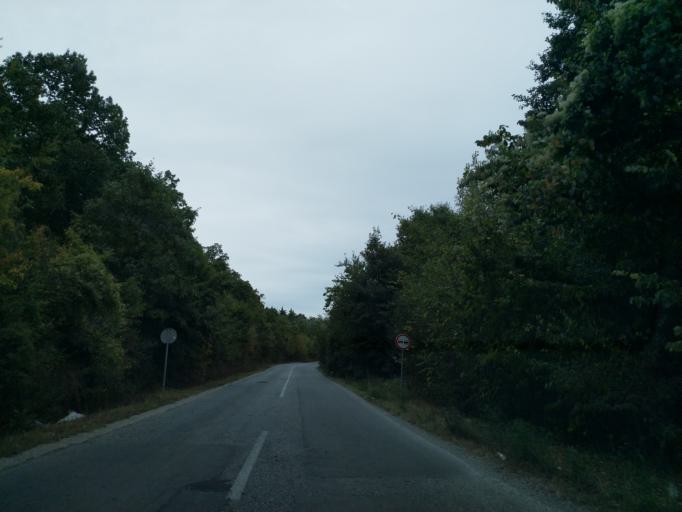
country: RS
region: Central Serbia
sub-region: Pomoravski Okrug
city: Jagodina
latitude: 44.0316
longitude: 21.1943
